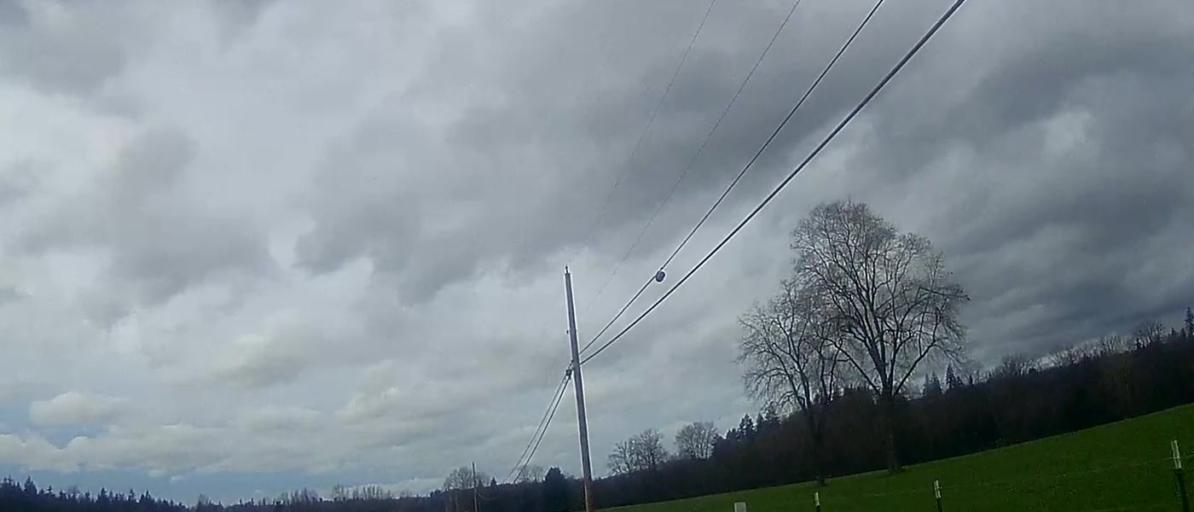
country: US
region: Washington
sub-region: Skagit County
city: Sedro-Woolley
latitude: 48.5835
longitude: -122.2635
